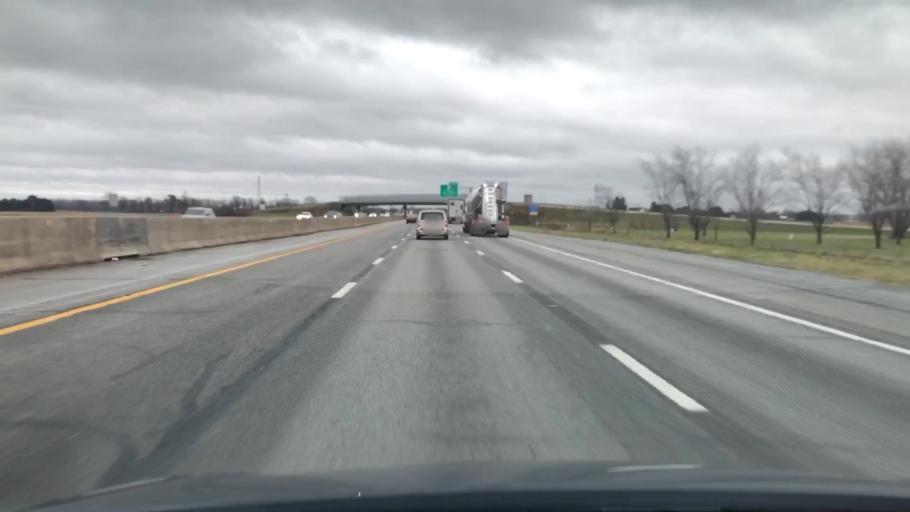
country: US
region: Ohio
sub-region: Sandusky County
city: Stony Prairie
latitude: 41.4162
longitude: -83.1549
